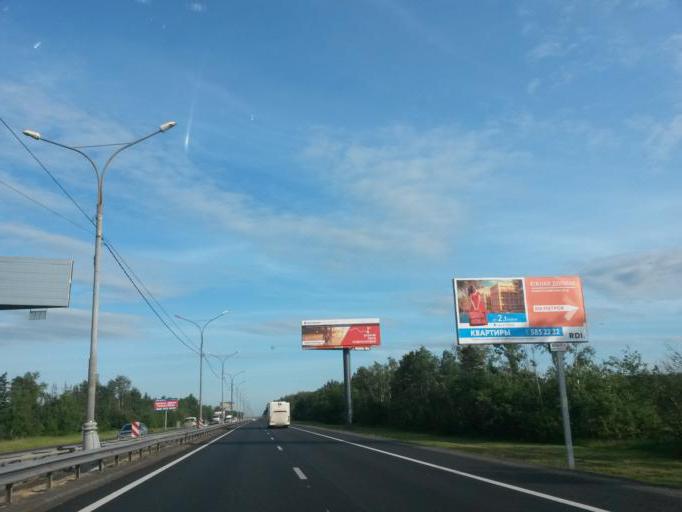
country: RU
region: Moskovskaya
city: Petrovskaya
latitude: 55.5226
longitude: 37.8210
